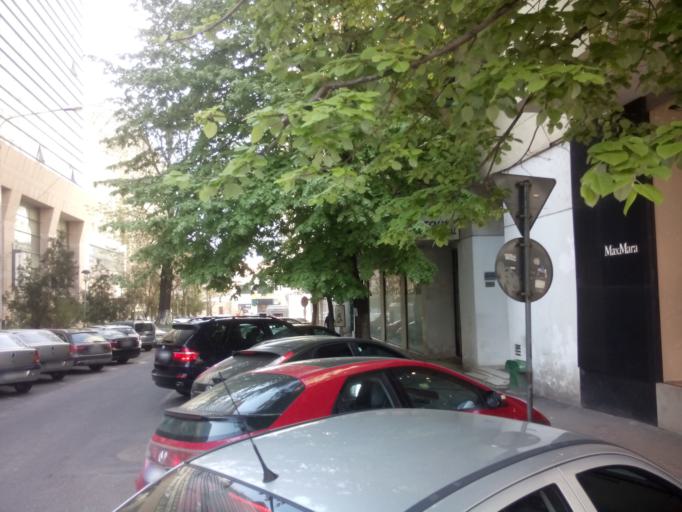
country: RO
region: Bucuresti
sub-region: Municipiul Bucuresti
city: Bucuresti
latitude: 44.4420
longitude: 26.0940
